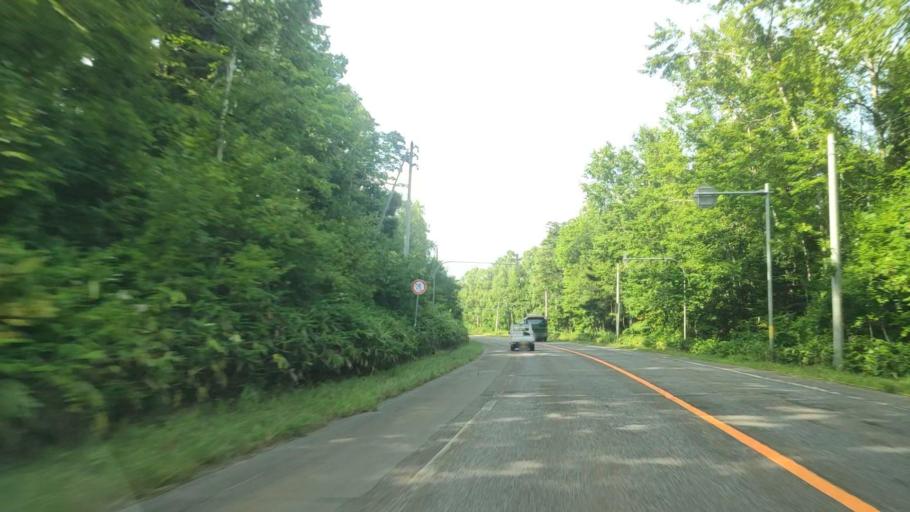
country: JP
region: Hokkaido
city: Nayoro
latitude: 44.3895
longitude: 142.3977
